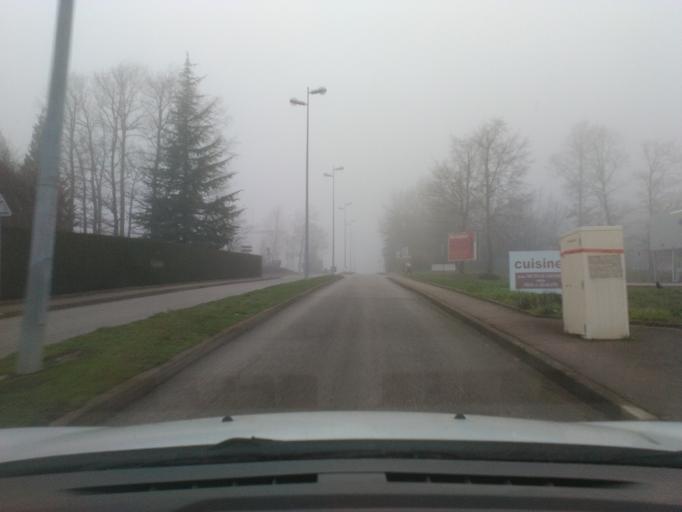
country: FR
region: Lorraine
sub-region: Departement des Vosges
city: Epinal
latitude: 48.1974
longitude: 6.4656
